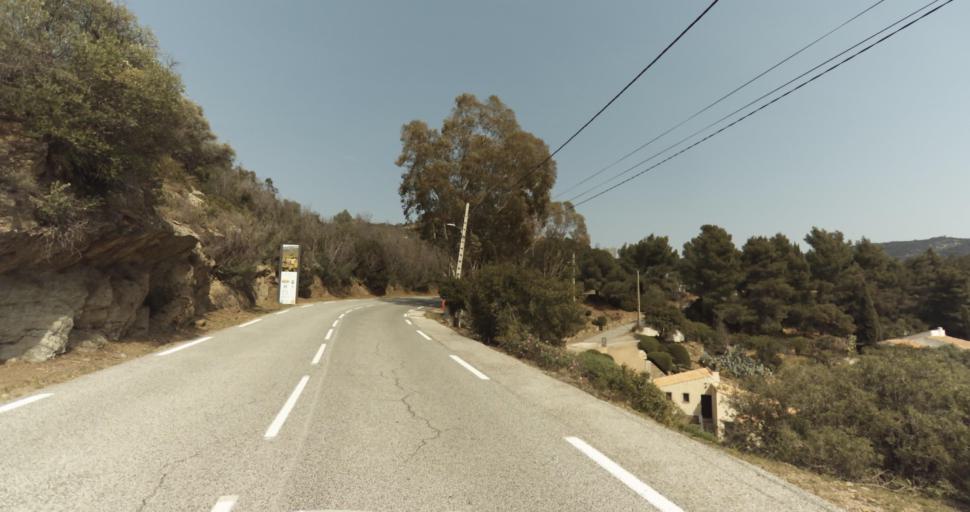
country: FR
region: Provence-Alpes-Cote d'Azur
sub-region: Departement du Var
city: Bormes-les-Mimosas
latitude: 43.1549
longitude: 6.3458
